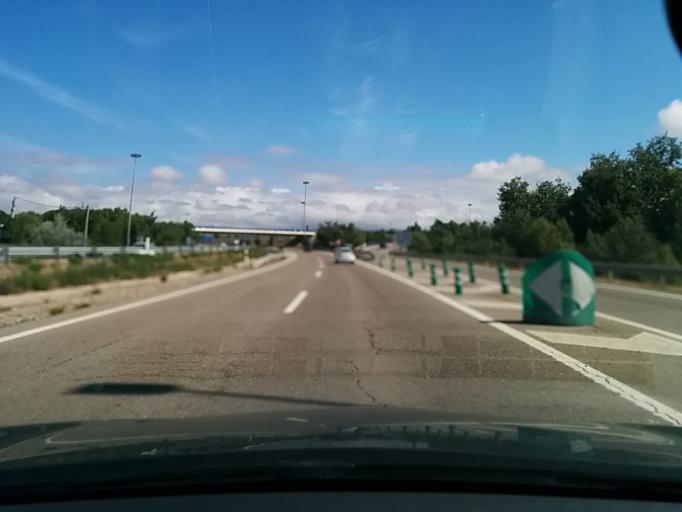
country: ES
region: Aragon
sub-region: Provincia de Huesca
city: Huesca
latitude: 42.1571
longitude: -0.4222
